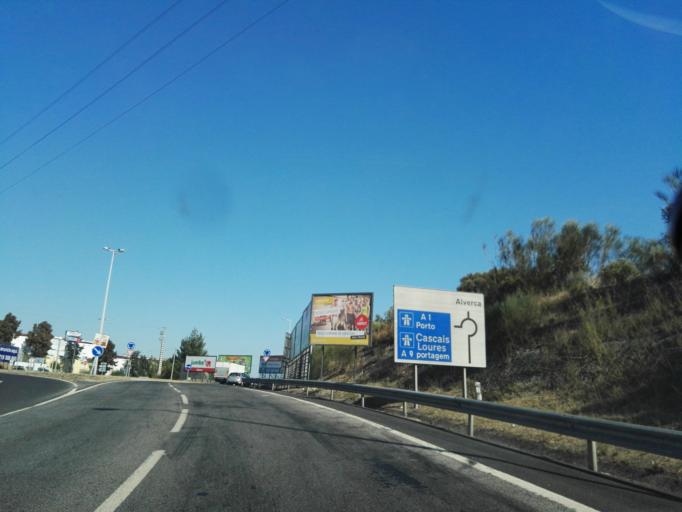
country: PT
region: Lisbon
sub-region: Vila Franca de Xira
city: Vialonga
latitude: 38.8911
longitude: -9.0487
